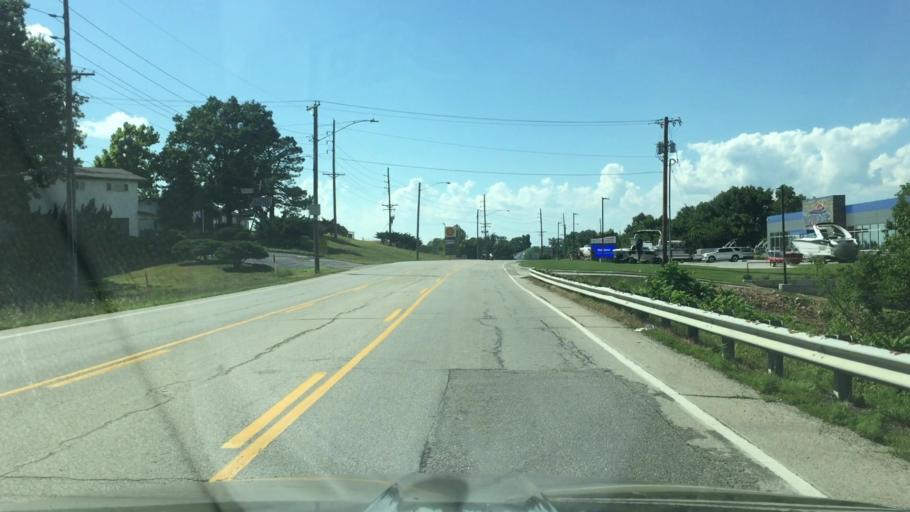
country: US
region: Missouri
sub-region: Miller County
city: Lake Ozark
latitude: 38.1764
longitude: -92.6180
